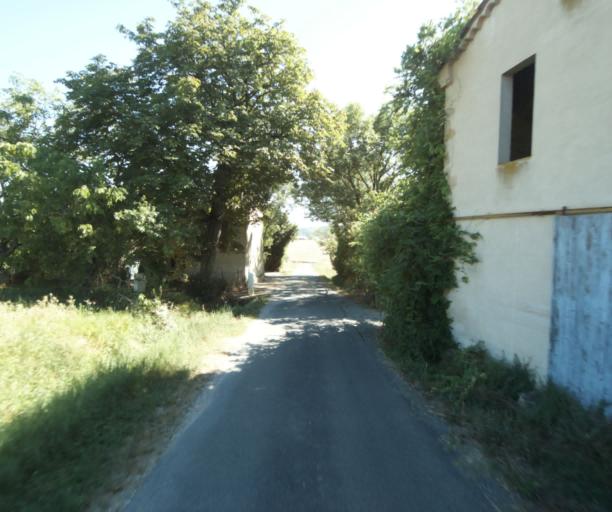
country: FR
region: Midi-Pyrenees
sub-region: Departement de la Haute-Garonne
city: Saint-Felix-Lauragais
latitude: 43.5156
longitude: 1.9114
